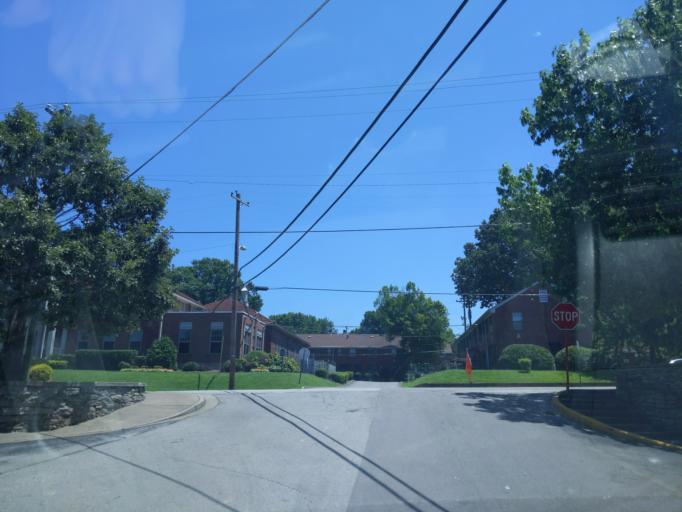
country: US
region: Tennessee
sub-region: Davidson County
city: Nashville
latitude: 36.1656
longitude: -86.7591
